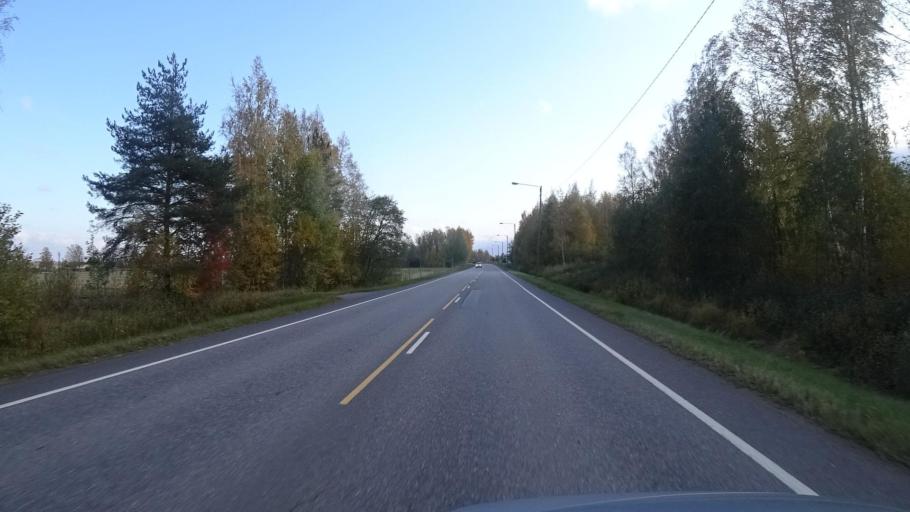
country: FI
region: Satakunta
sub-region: Rauma
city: Saekylae
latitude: 61.0619
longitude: 22.3254
